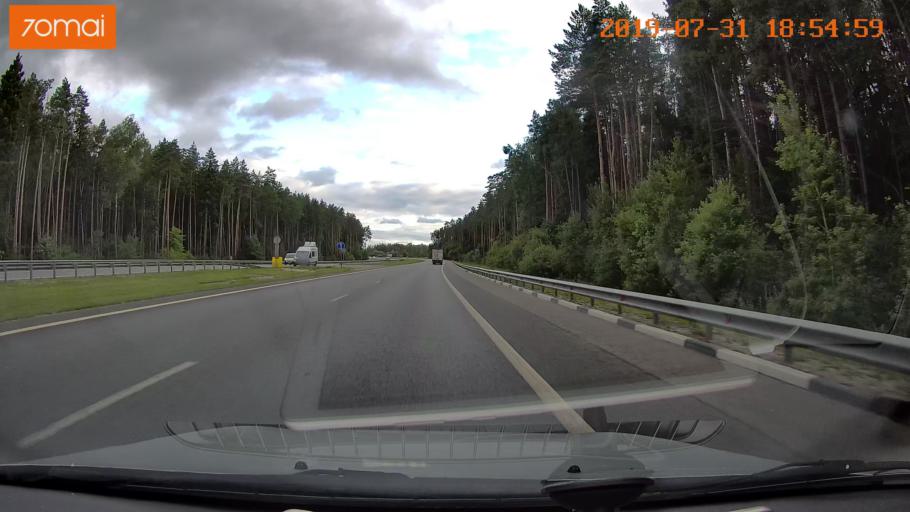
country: RU
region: Moskovskaya
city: Raduzhnyy
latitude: 55.1815
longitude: 38.6687
